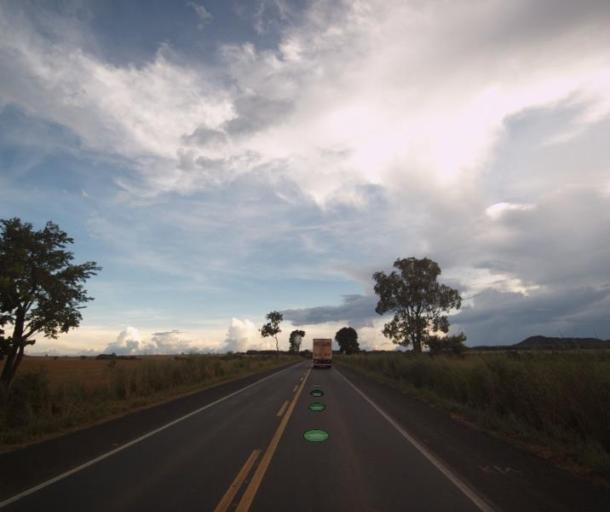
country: BR
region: Goias
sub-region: Uruacu
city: Uruacu
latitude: -14.1450
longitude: -49.1168
